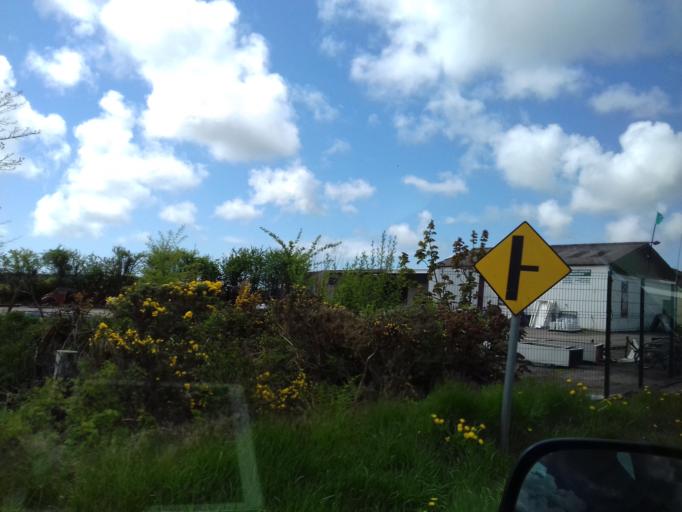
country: IE
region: Leinster
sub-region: Loch Garman
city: Loch Garman
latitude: 52.2884
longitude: -6.6151
